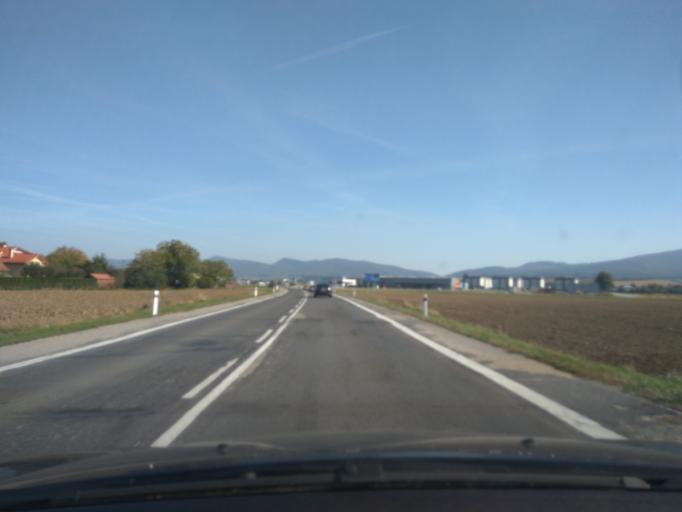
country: SK
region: Trenciansky
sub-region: Okres Trencin
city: Trencin
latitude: 48.8493
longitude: 17.9819
